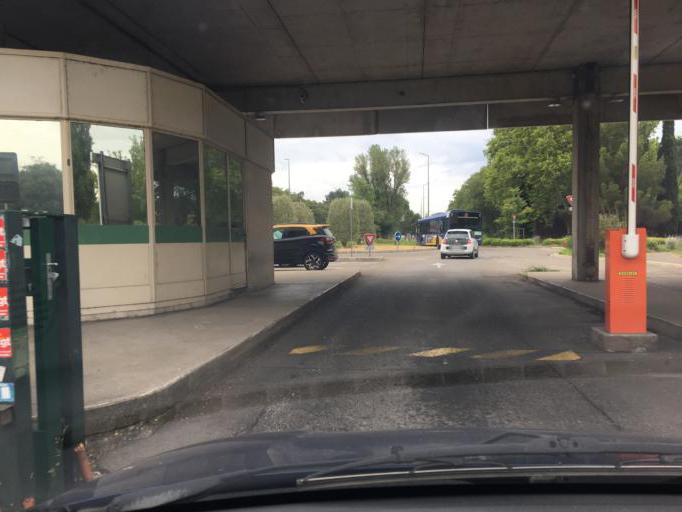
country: FR
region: Provence-Alpes-Cote d'Azur
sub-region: Departement des Bouches-du-Rhone
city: Rognonas
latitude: 43.9204
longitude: 4.8052
